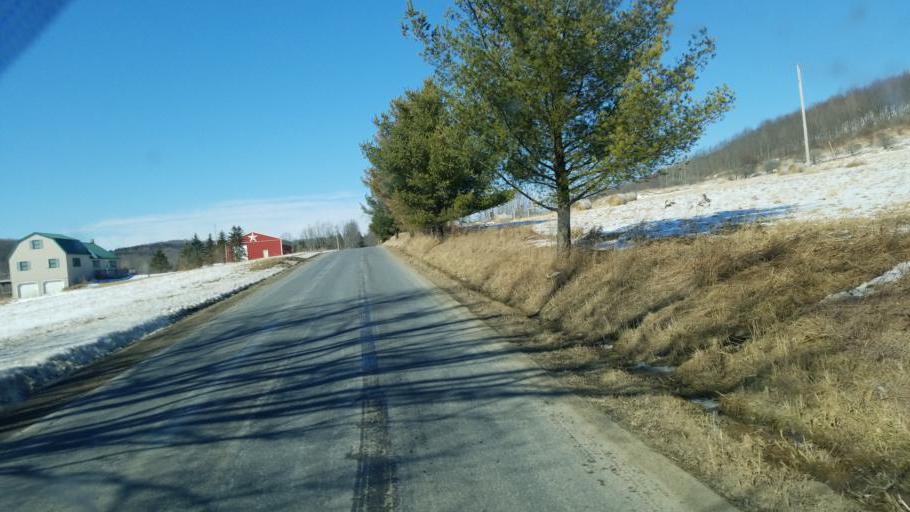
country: US
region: Pennsylvania
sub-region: Tioga County
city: Westfield
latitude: 41.9766
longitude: -77.6646
